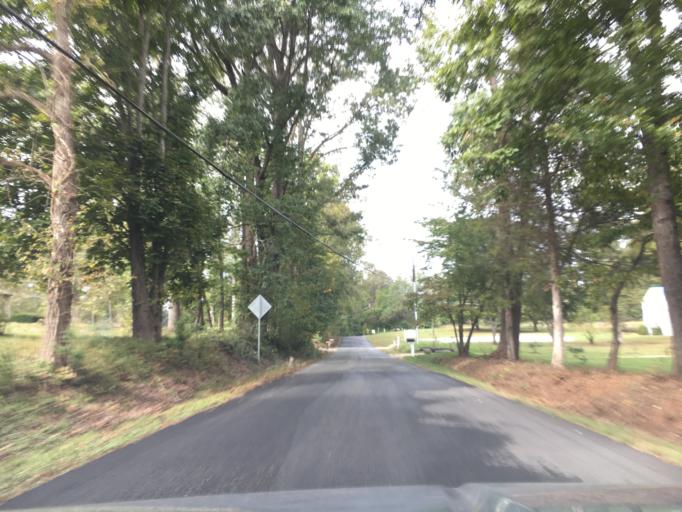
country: US
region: Virginia
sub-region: Goochland County
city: Goochland
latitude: 37.7015
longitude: -77.8358
